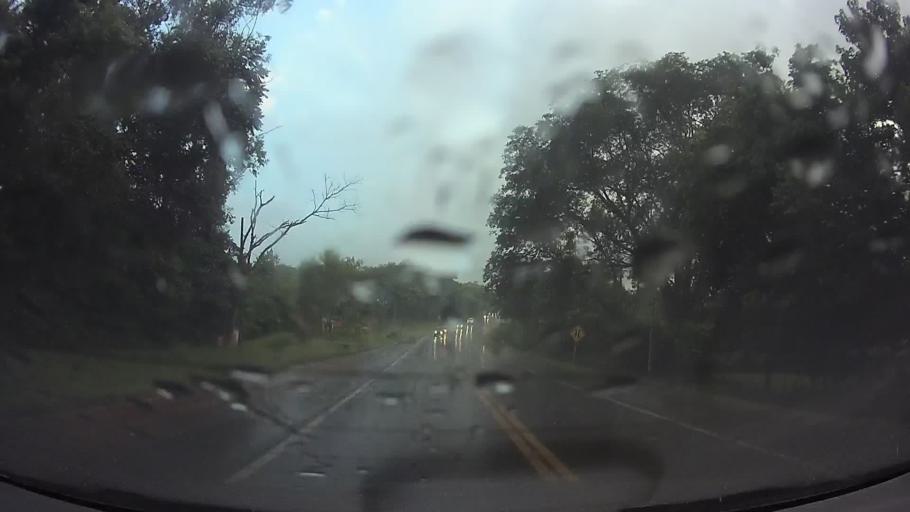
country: PY
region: Paraguari
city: Yaguaron
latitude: -25.5860
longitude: -57.2390
